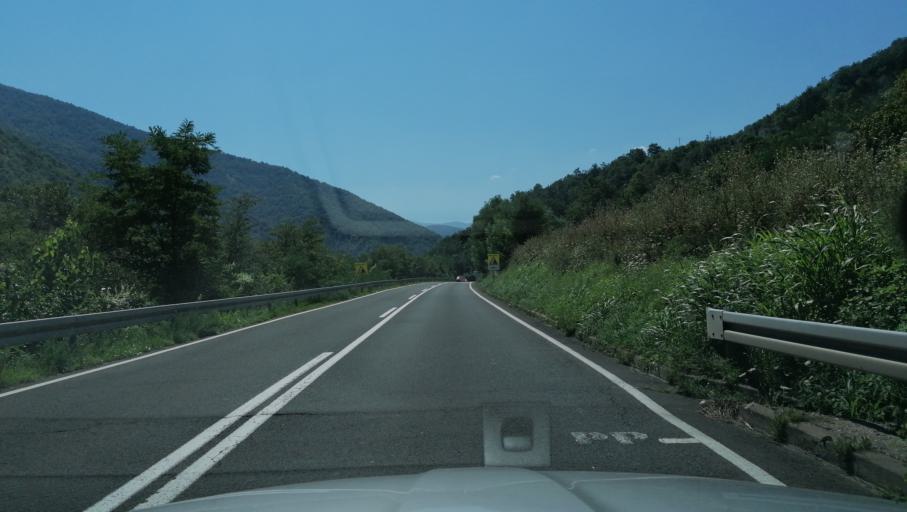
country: RS
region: Central Serbia
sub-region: Raski Okrug
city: Kraljevo
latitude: 43.6446
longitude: 20.5520
